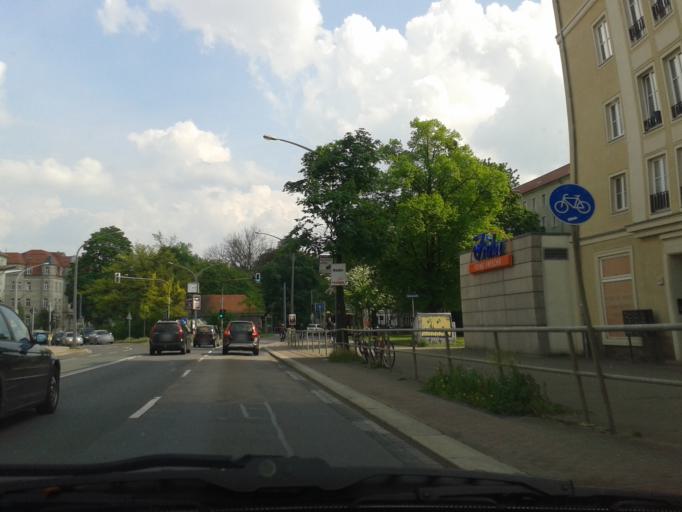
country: DE
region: Saxony
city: Dresden
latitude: 51.0345
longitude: 13.7210
